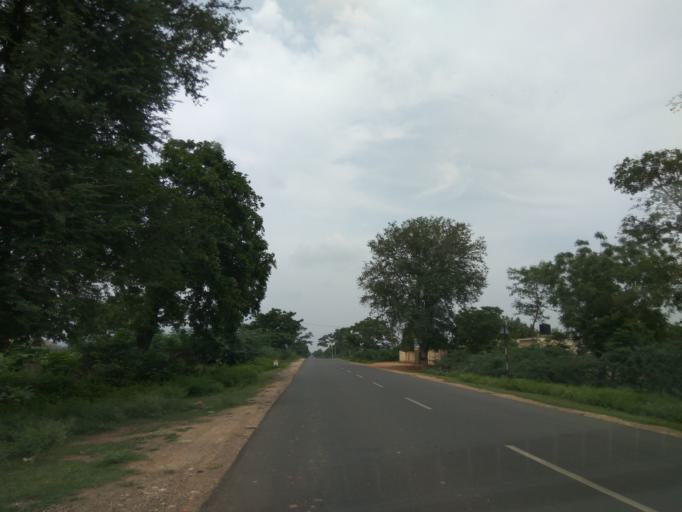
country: IN
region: Andhra Pradesh
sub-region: Prakasam
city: Cumbum
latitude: 15.5038
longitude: 79.0858
